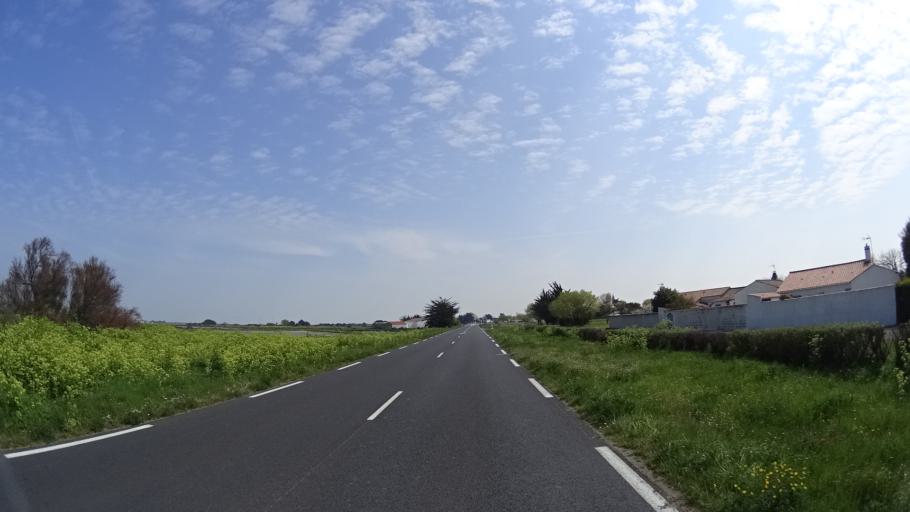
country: FR
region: Pays de la Loire
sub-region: Departement de la Vendee
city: La Gueriniere
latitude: 46.9839
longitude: -2.2702
